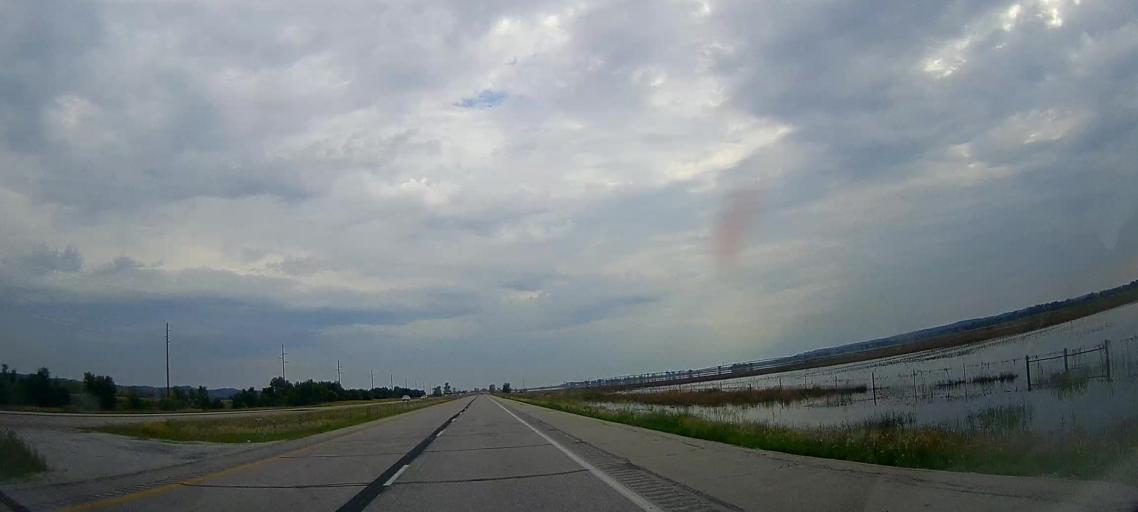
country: US
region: Iowa
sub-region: Harrison County
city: Missouri Valley
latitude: 41.4540
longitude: -95.8997
